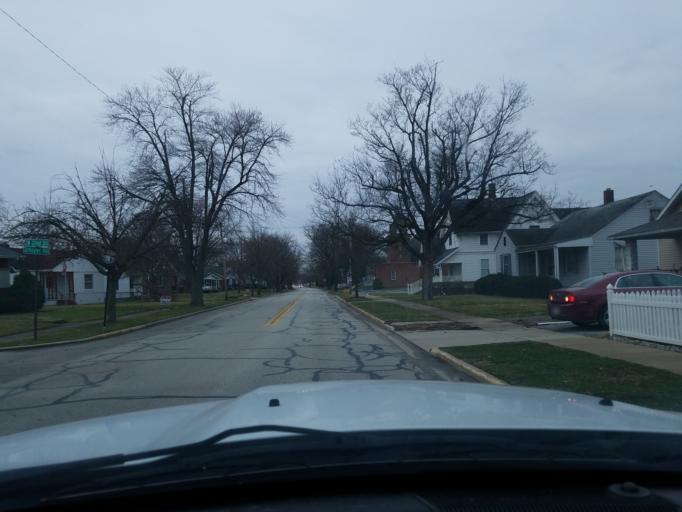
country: US
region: Indiana
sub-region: Tippecanoe County
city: Lafayette
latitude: 40.4427
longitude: -86.8720
